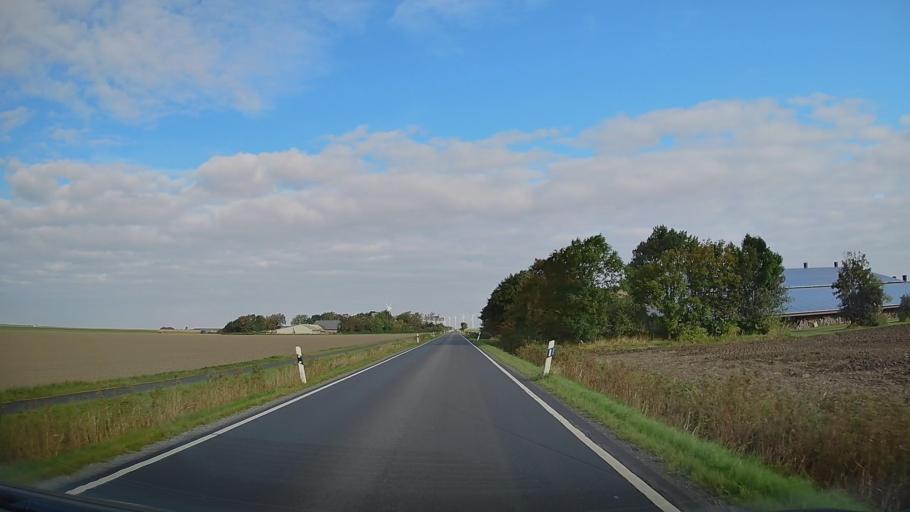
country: DE
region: Schleswig-Holstein
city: Reussenkoge
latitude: 54.5759
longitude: 8.9273
